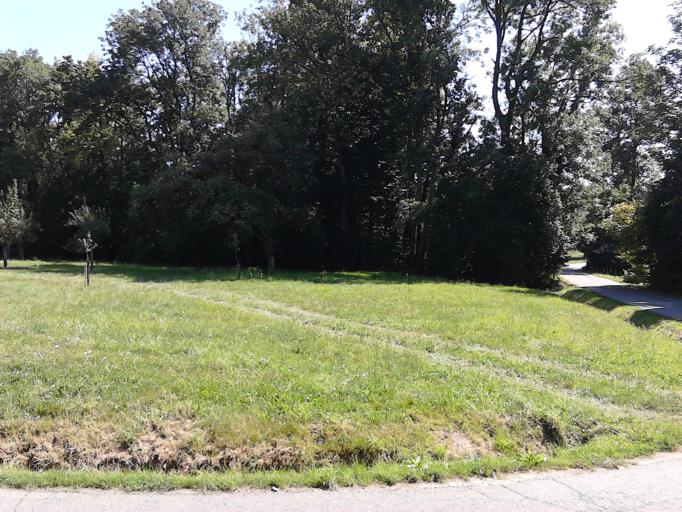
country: DE
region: Baden-Wuerttemberg
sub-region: Tuebingen Region
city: Markdorf
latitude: 47.6814
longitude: 9.4129
